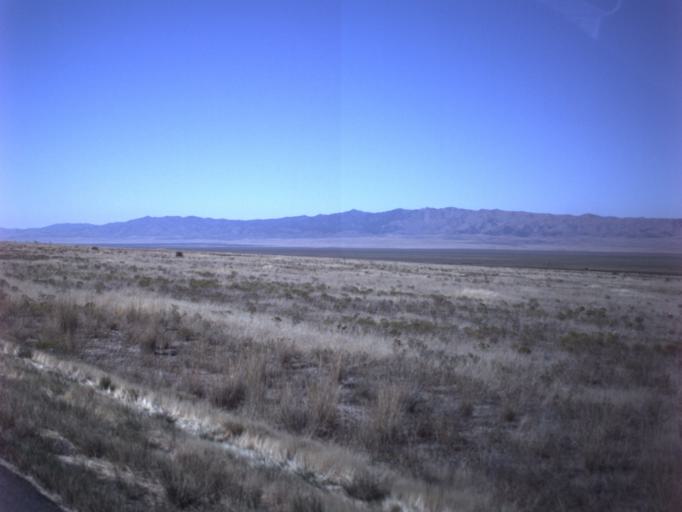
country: US
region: Utah
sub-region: Tooele County
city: Grantsville
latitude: 40.5974
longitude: -112.7158
